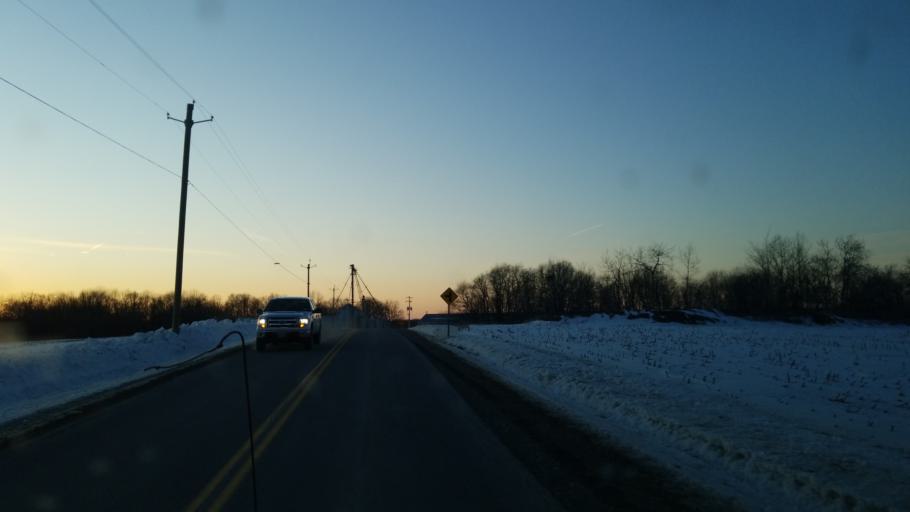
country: US
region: New York
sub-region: Allegany County
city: Andover
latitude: 42.0085
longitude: -77.7028
